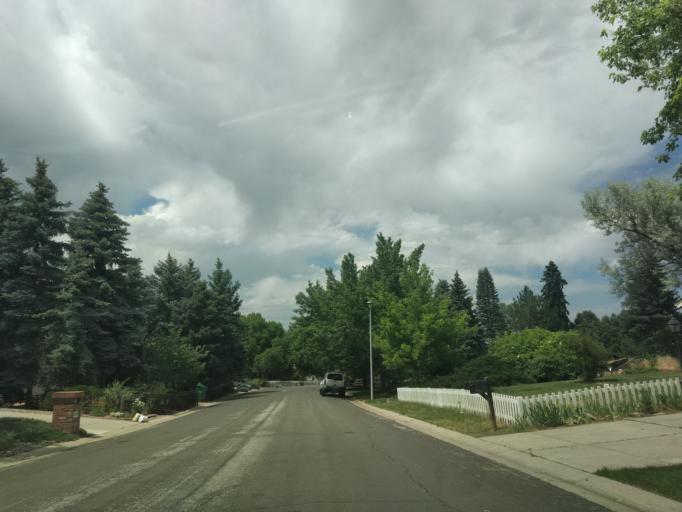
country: US
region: Colorado
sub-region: Jefferson County
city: Lakewood
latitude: 39.6833
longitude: -105.1263
